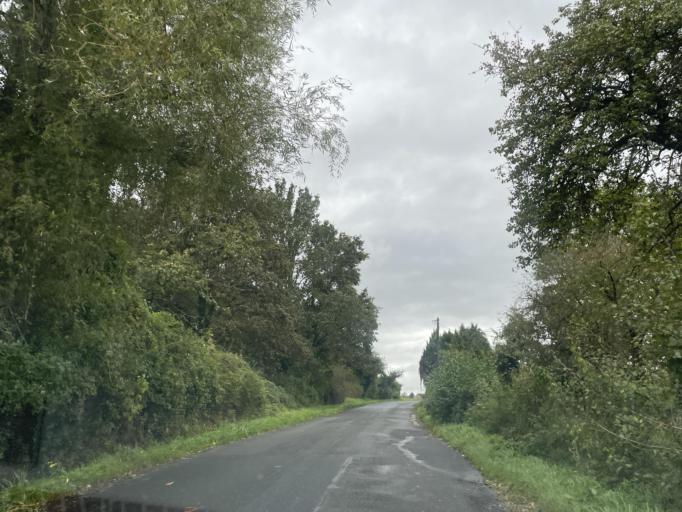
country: FR
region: Ile-de-France
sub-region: Departement de Seine-et-Marne
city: Coulommiers
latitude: 48.8176
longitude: 3.1054
